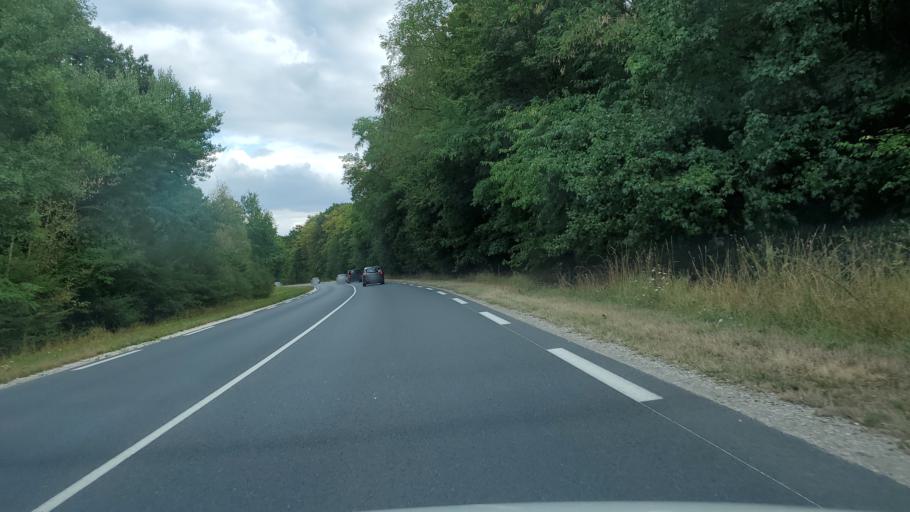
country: FR
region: Ile-de-France
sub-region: Departement de Seine-et-Marne
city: Villeneuve-le-Comte
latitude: 48.8055
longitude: 2.8432
